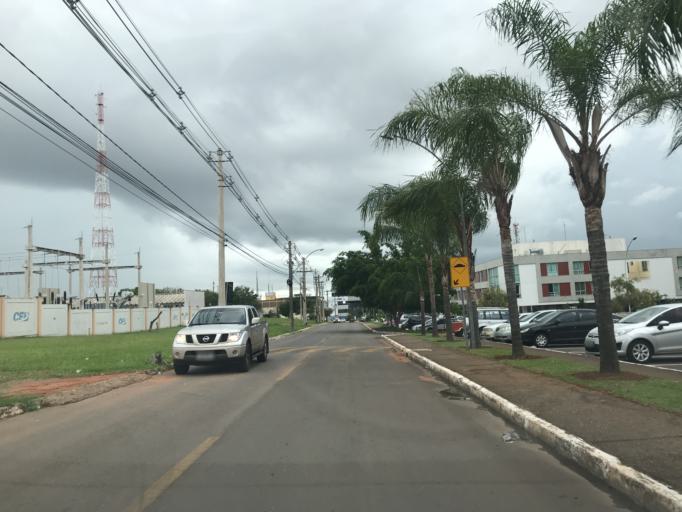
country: BR
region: Federal District
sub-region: Brasilia
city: Brasilia
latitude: -15.7871
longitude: -47.9167
